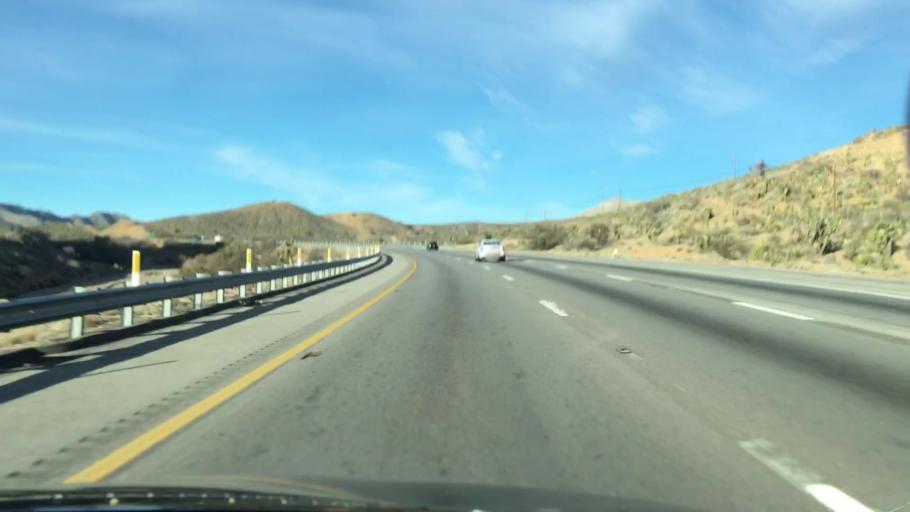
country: US
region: Nevada
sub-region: Clark County
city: Sandy Valley
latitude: 35.4709
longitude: -115.5025
